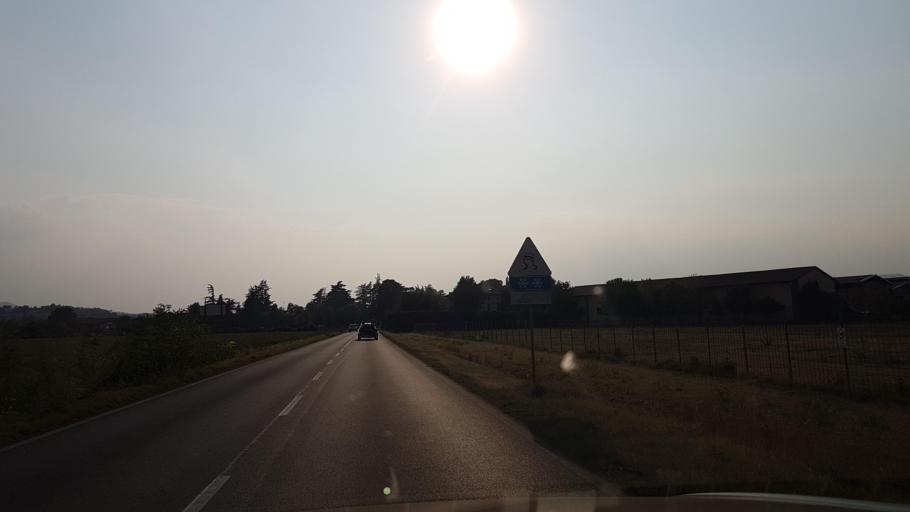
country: IT
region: Emilia-Romagna
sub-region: Provincia di Parma
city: Gaiano
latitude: 44.7186
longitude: 10.1580
